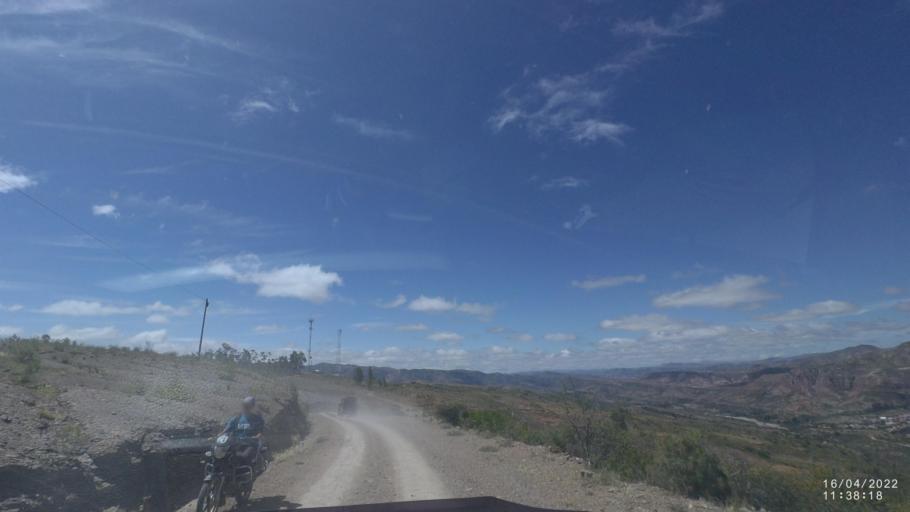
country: BO
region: Cochabamba
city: Mizque
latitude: -17.9639
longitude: -65.6389
